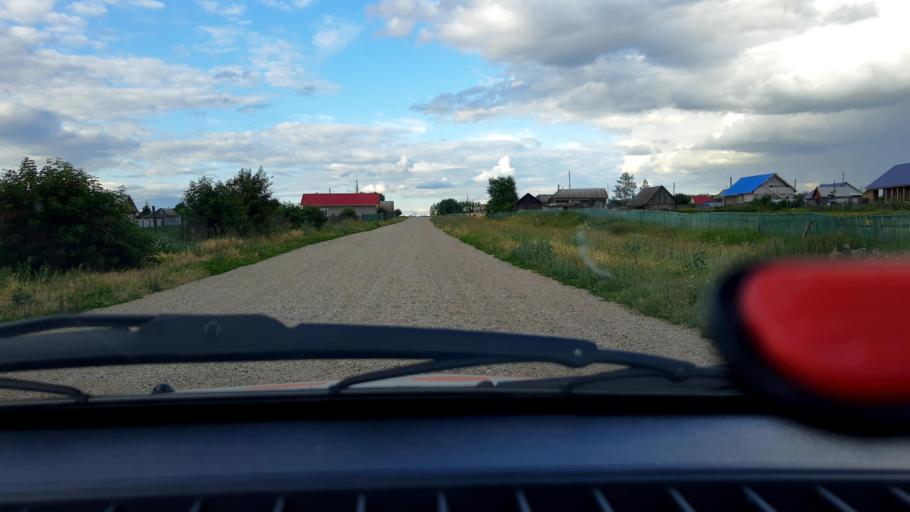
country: RU
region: Bashkortostan
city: Karmaskaly
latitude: 54.4217
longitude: 56.0233
